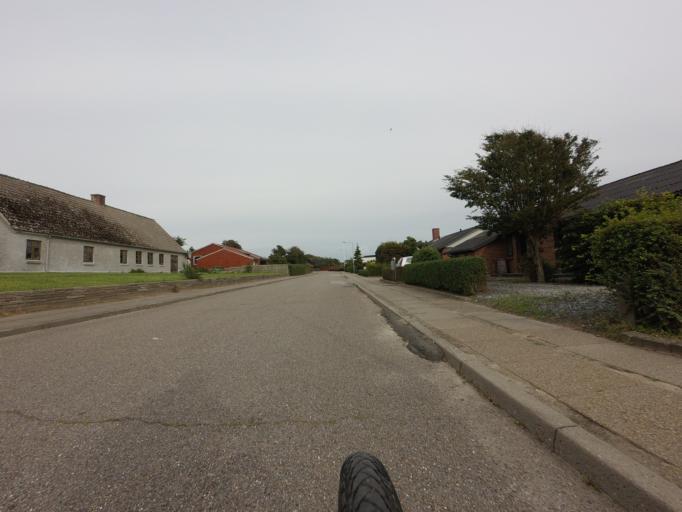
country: DK
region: North Denmark
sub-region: Hjorring Kommune
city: Vra
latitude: 57.4261
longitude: 9.8402
